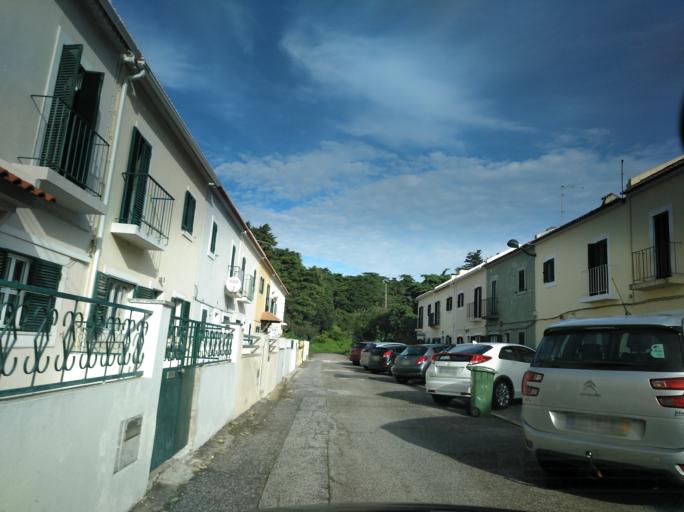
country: PT
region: Lisbon
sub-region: Oeiras
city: Alges
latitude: 38.7133
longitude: -9.2045
